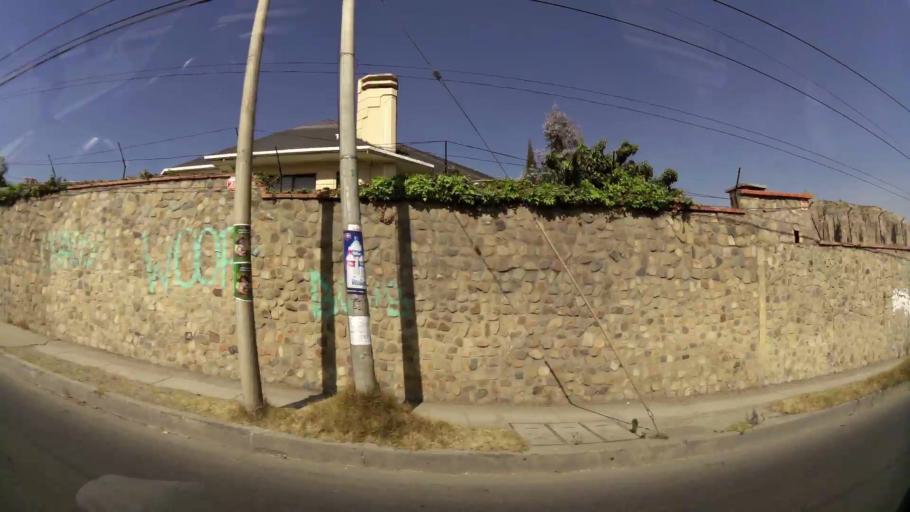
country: BO
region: La Paz
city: La Paz
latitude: -16.5261
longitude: -68.0681
